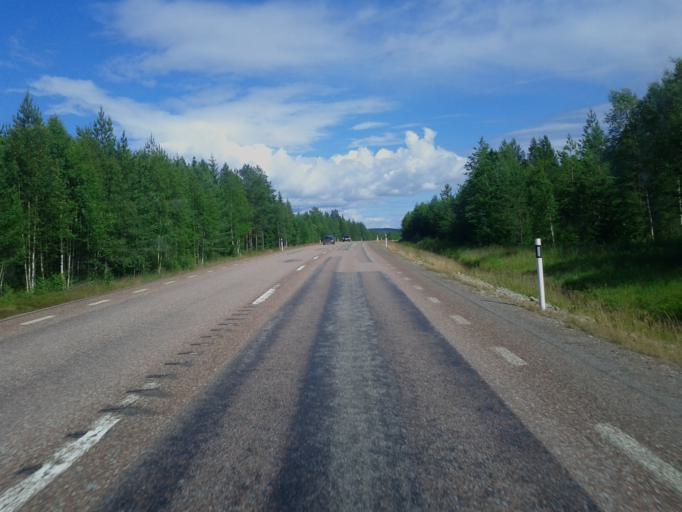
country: SE
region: Dalarna
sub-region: Rattviks Kommun
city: Raettvik
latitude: 60.8447
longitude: 15.1781
